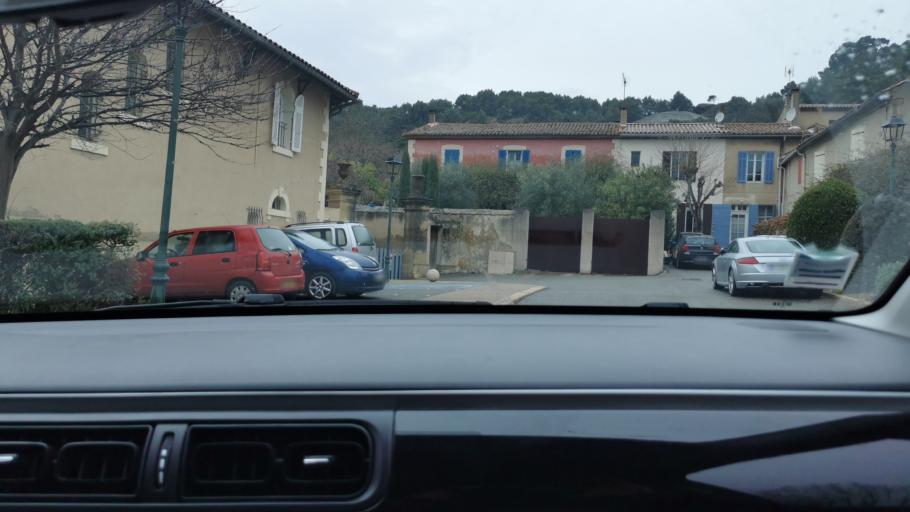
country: FR
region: Provence-Alpes-Cote d'Azur
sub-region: Departement des Bouches-du-Rhone
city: Lamanon
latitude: 43.7010
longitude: 5.0838
